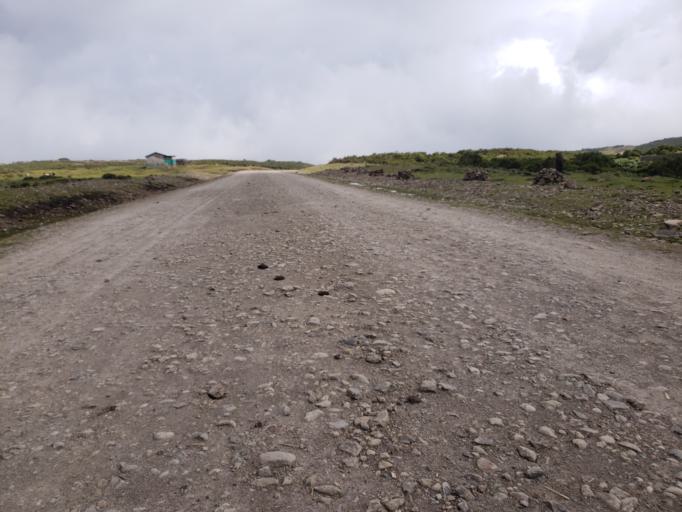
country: ET
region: Oromiya
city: Dodola
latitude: 6.7597
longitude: 39.4274
